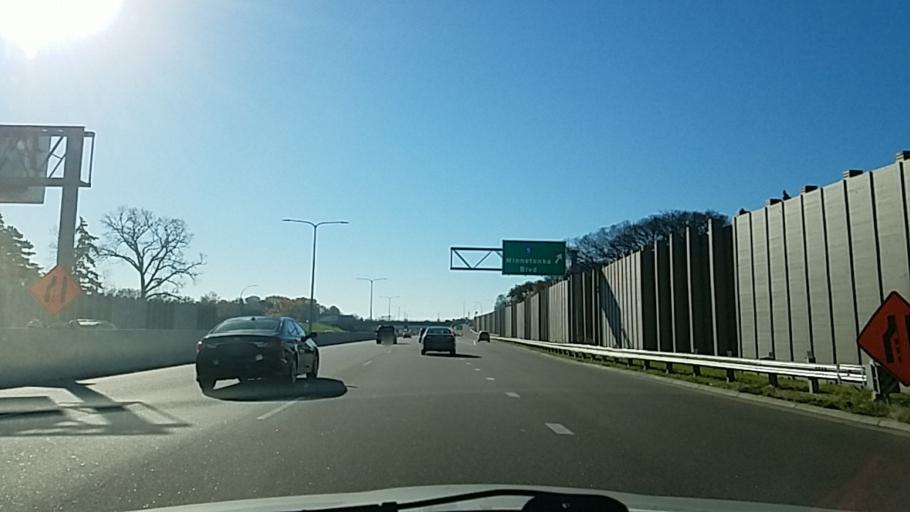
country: US
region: Minnesota
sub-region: Hennepin County
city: Saint Louis Park
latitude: 44.9522
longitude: -93.3480
